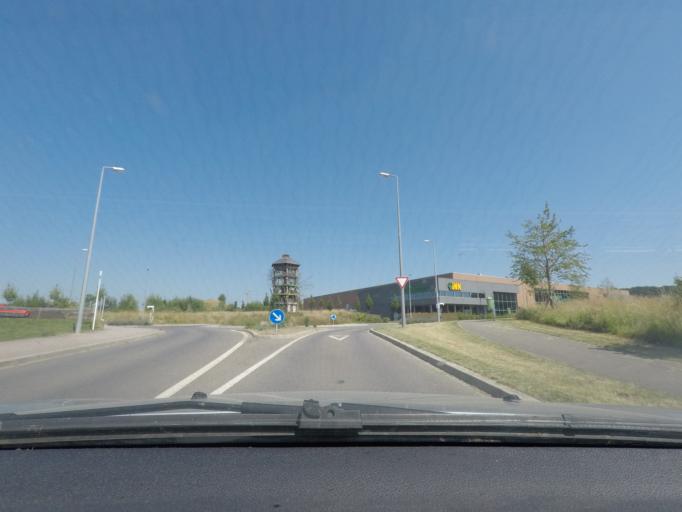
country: LU
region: Diekirch
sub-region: Canton de Redange
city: Redange-sur-Attert
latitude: 49.7704
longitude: 5.8971
